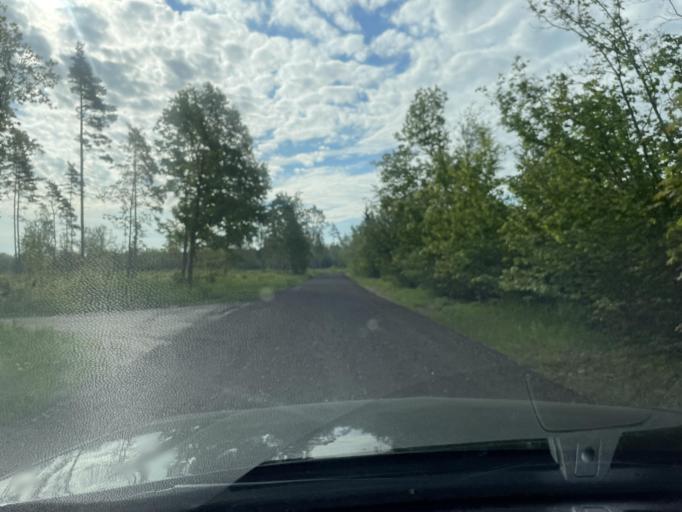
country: EE
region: Harju
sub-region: Keila linn
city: Keila
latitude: 59.3084
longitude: 24.2876
